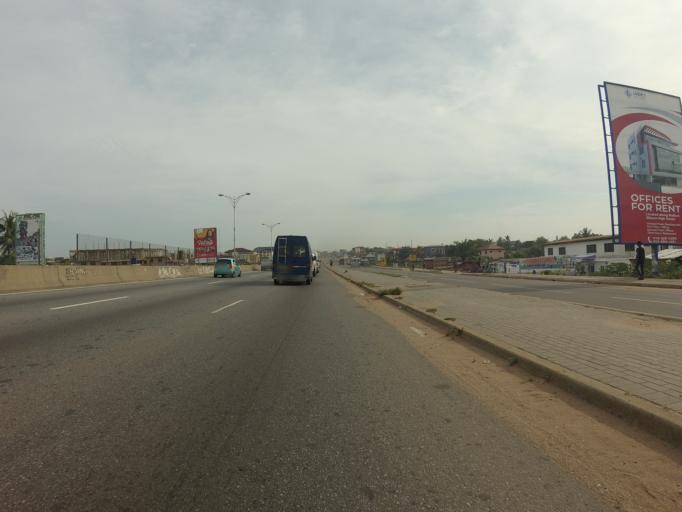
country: GH
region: Greater Accra
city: Gbawe
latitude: 5.5945
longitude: -0.2663
